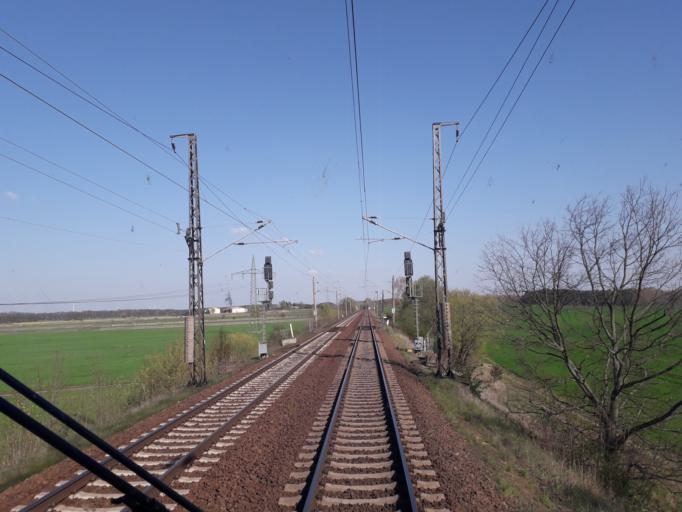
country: DE
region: Brandenburg
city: Stahnsdorf
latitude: 52.3220
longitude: 13.1554
